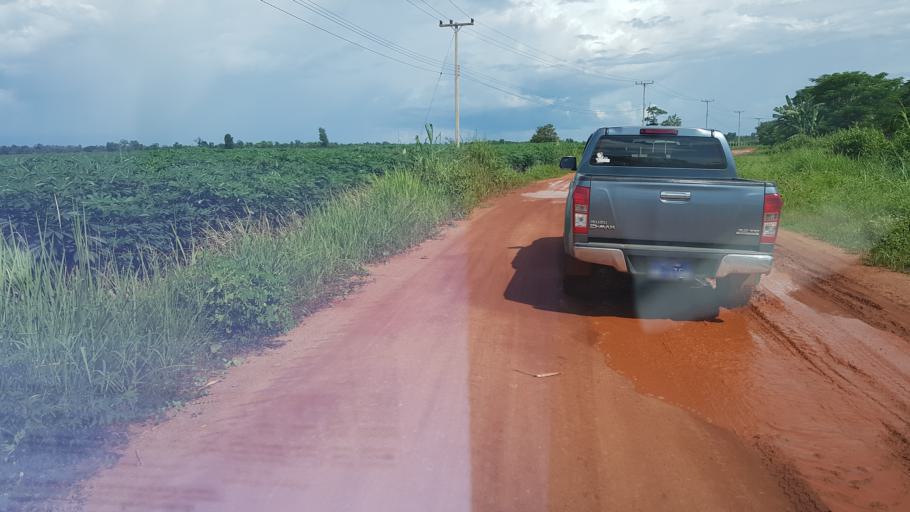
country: LA
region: Vientiane
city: Vientiane
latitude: 18.2226
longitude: 102.5685
